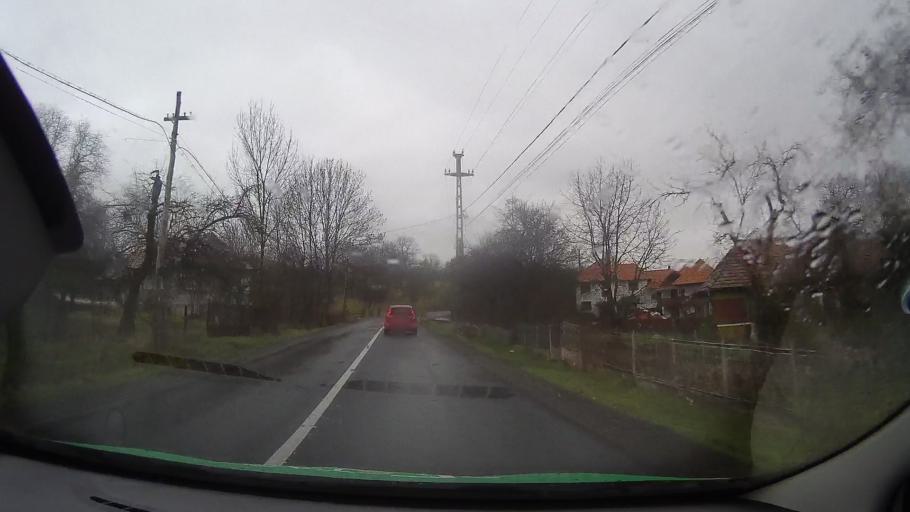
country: RO
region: Mures
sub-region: Comuna Vatava
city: Vatava
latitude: 46.9476
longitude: 24.7619
